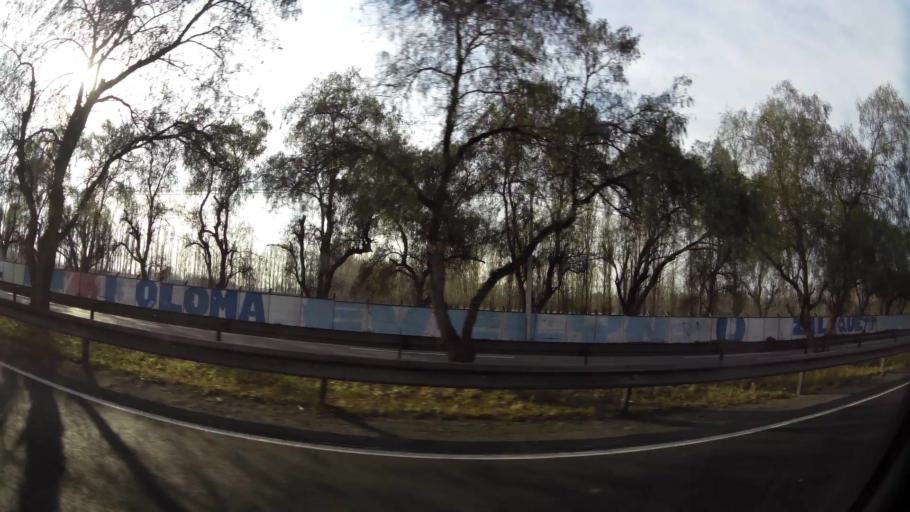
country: CL
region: Santiago Metropolitan
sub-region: Provincia de Talagante
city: Penaflor
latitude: -33.6256
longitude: -70.8628
